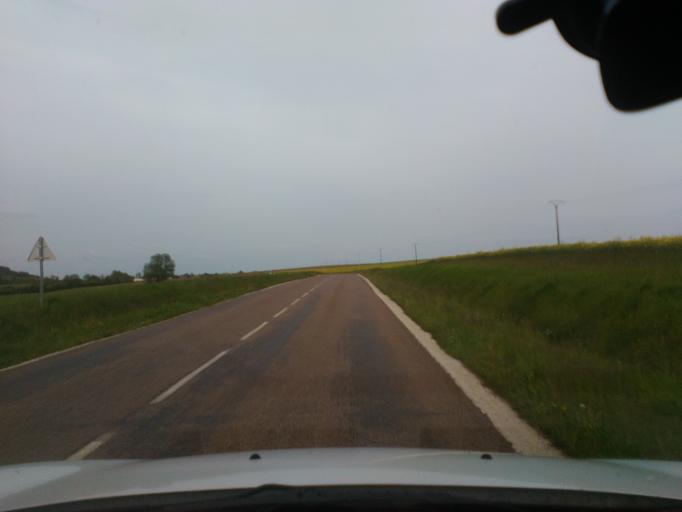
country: FR
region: Champagne-Ardenne
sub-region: Departement de la Haute-Marne
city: Bologne
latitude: 48.2136
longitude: 5.2221
